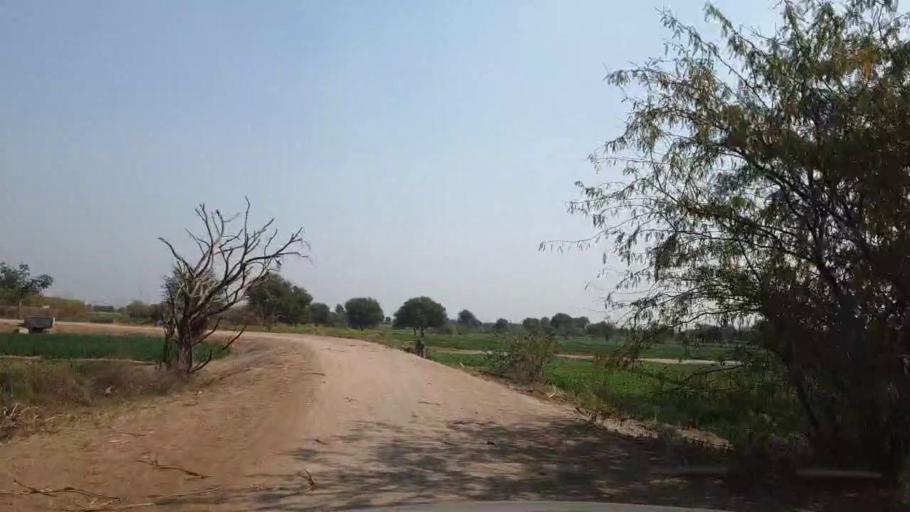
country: PK
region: Sindh
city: Tando Allahyar
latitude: 25.5541
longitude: 68.7197
